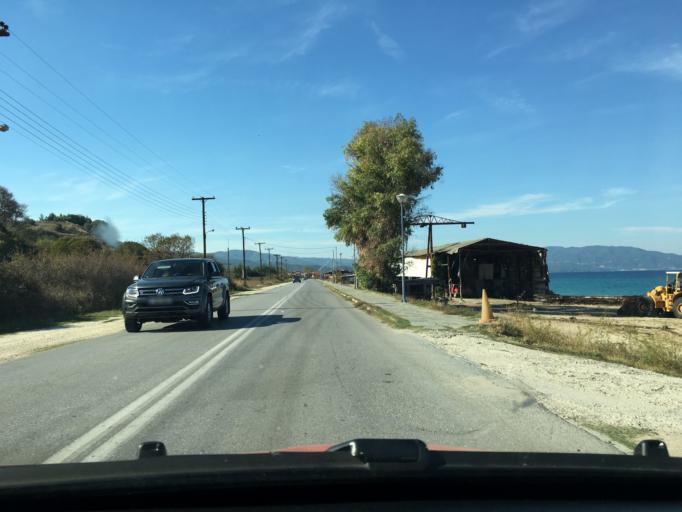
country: GR
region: Central Macedonia
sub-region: Nomos Chalkidikis
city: Ierissos
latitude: 40.3944
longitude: 23.8898
